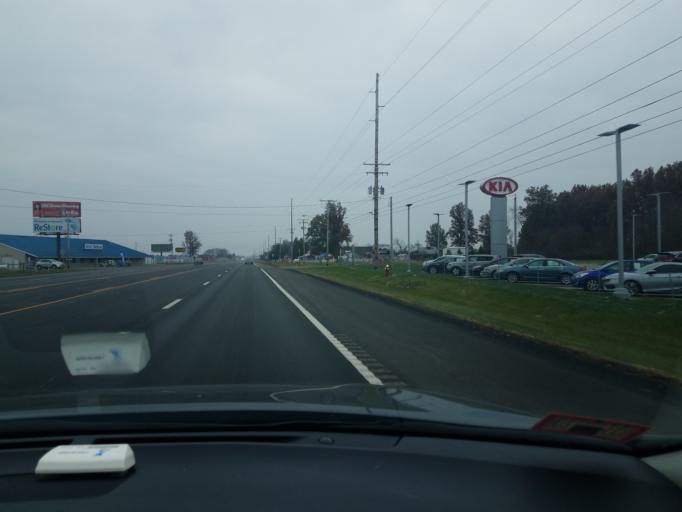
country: US
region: Ohio
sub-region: Erie County
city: Milan
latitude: 41.3787
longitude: -82.6444
